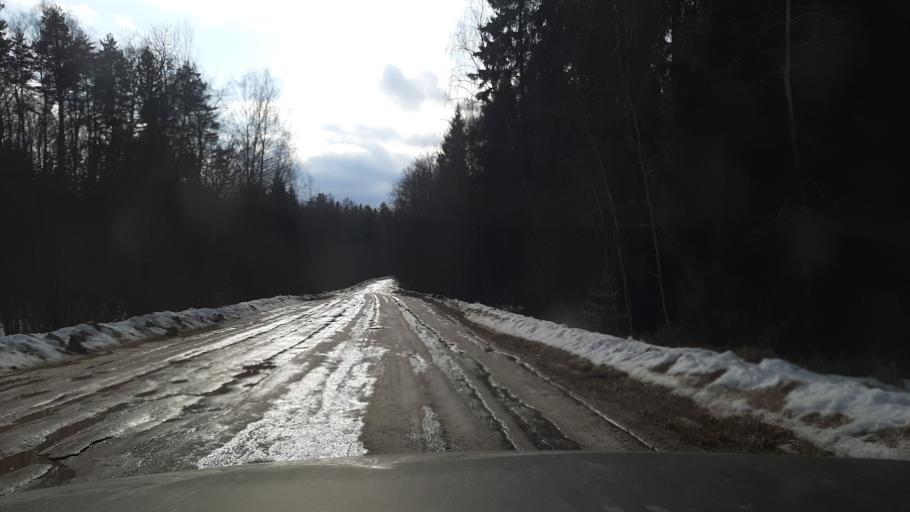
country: RU
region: Ivanovo
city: Teykovo
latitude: 56.8888
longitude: 40.6568
